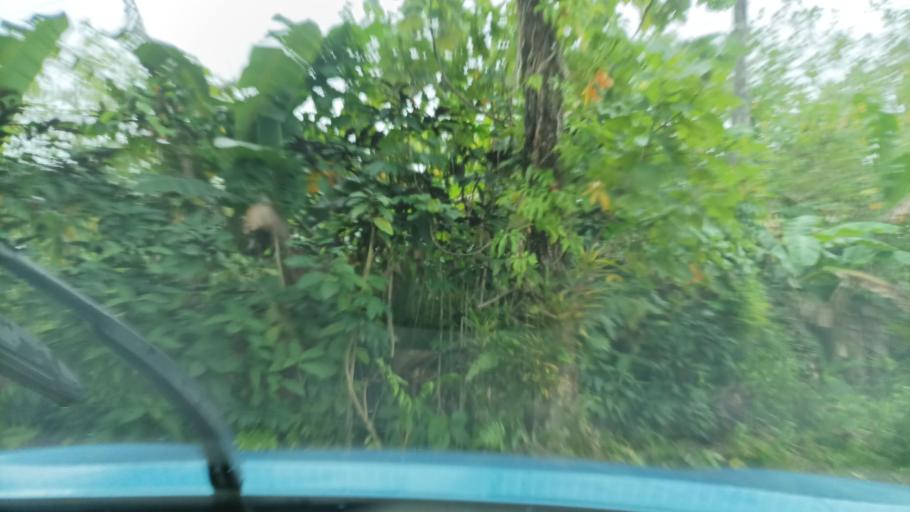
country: FM
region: Pohnpei
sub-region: Kolonia Municipality
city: Kolonia
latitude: 6.9561
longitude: 158.2216
